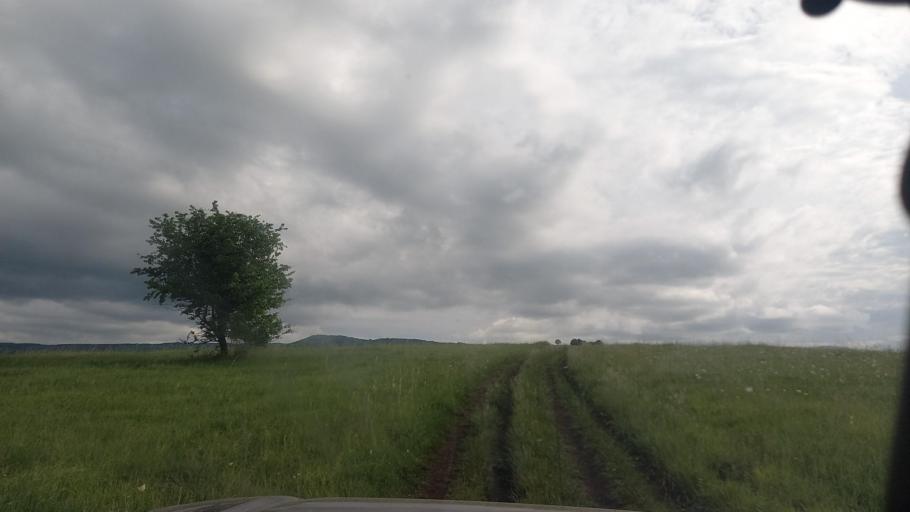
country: RU
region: Krasnodarskiy
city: Peredovaya
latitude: 44.0761
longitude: 41.3666
